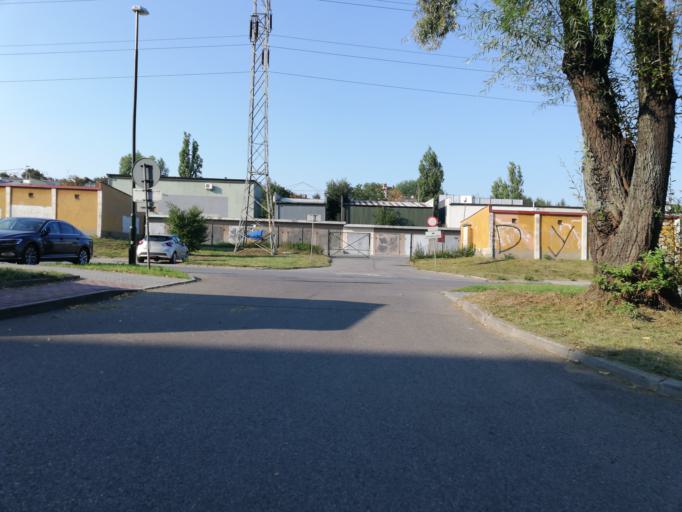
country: PL
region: Lesser Poland Voivodeship
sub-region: Krakow
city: Krakow
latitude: 50.0858
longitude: 20.0089
